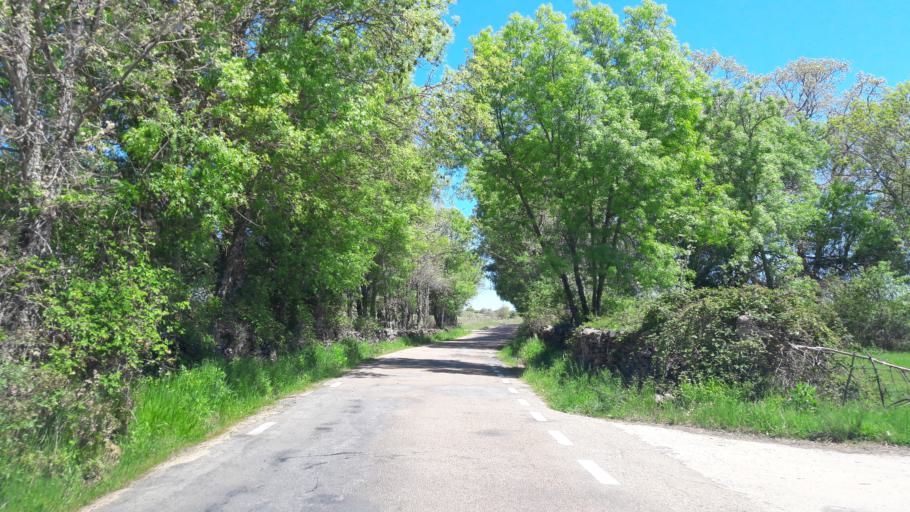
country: ES
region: Castille and Leon
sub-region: Provincia de Salamanca
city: Endrinal
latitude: 40.5652
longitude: -5.8092
